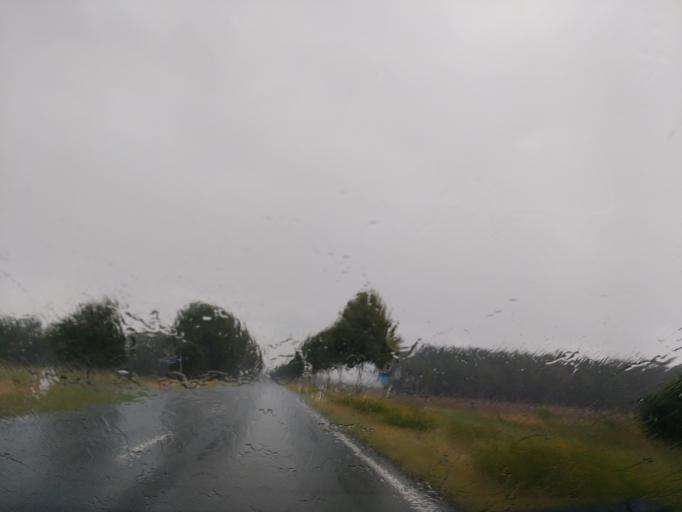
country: DE
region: North Rhine-Westphalia
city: Lengerich
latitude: 52.1218
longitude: 7.8244
